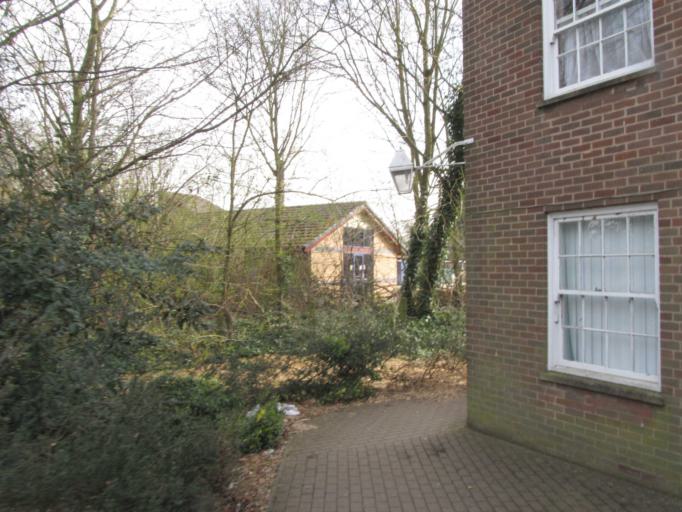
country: GB
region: England
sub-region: Nottingham
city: Nottingham
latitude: 52.9418
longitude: -1.1944
